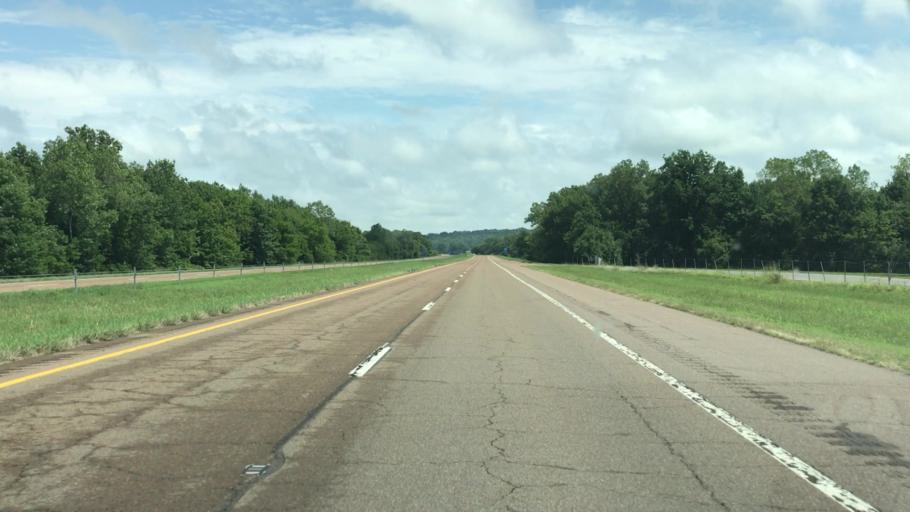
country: US
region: Tennessee
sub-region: Dyer County
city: Dyersburg
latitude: 36.0797
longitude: -89.5249
